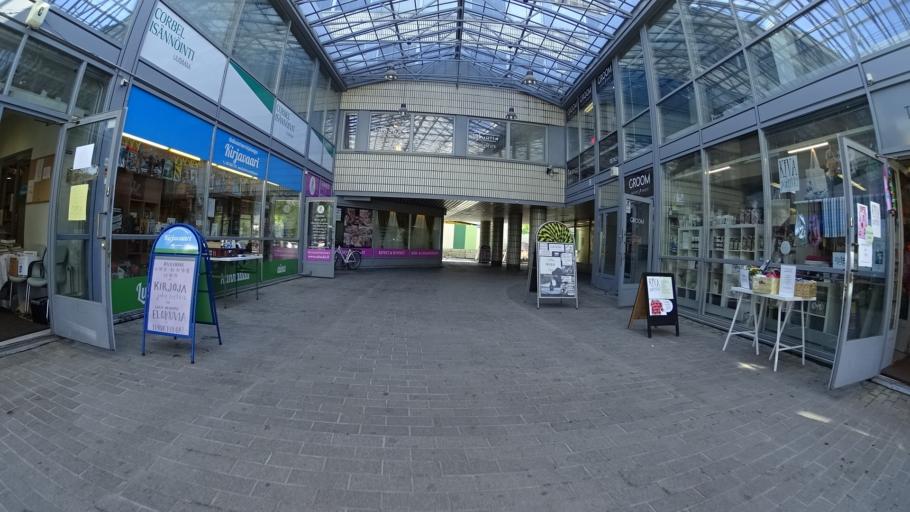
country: FI
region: Uusimaa
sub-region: Helsinki
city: Jaervenpaeae
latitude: 60.4718
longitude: 25.0878
